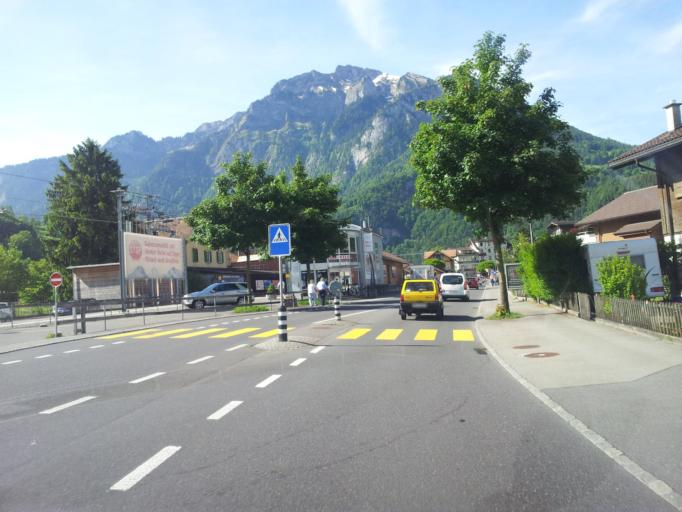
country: CH
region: Bern
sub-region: Interlaken-Oberhasli District
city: Wilderswil
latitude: 46.6672
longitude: 7.8700
